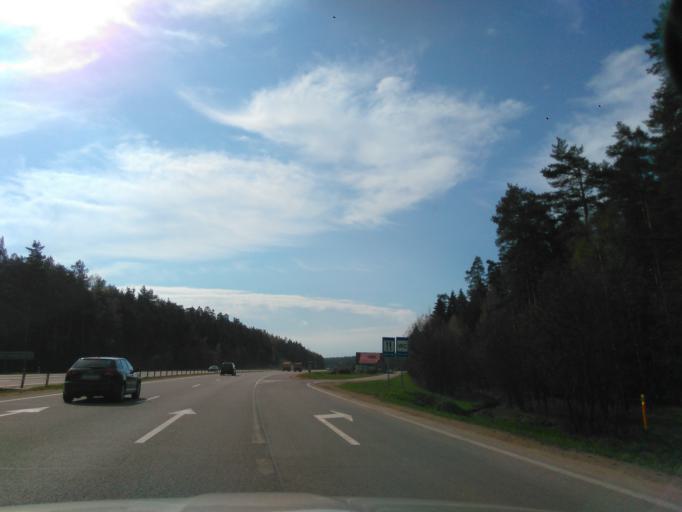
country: BY
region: Minsk
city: Rakaw
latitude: 53.9553
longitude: 27.1137
